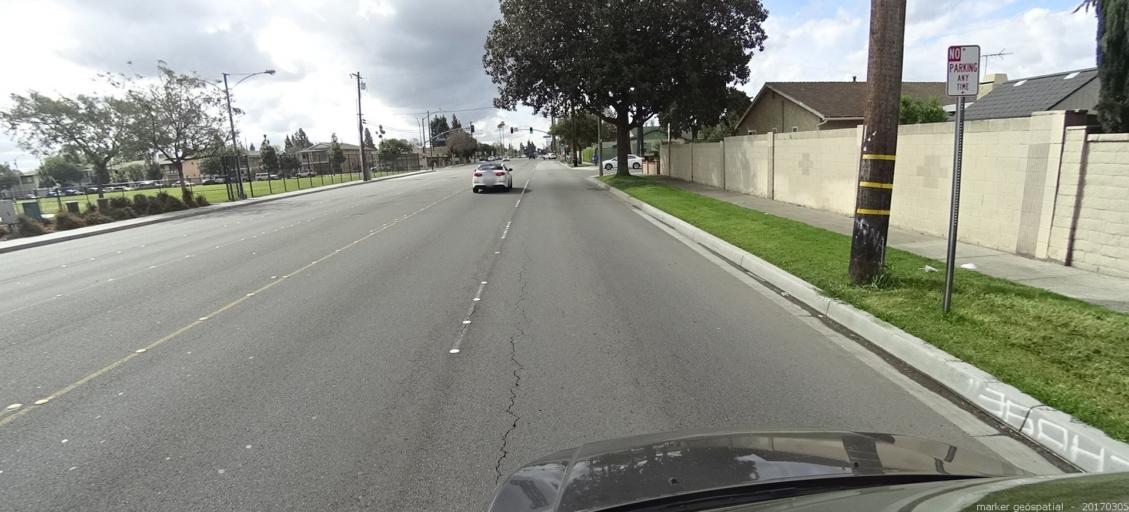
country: US
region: California
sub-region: Orange County
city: Garden Grove
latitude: 33.7949
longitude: -117.9065
